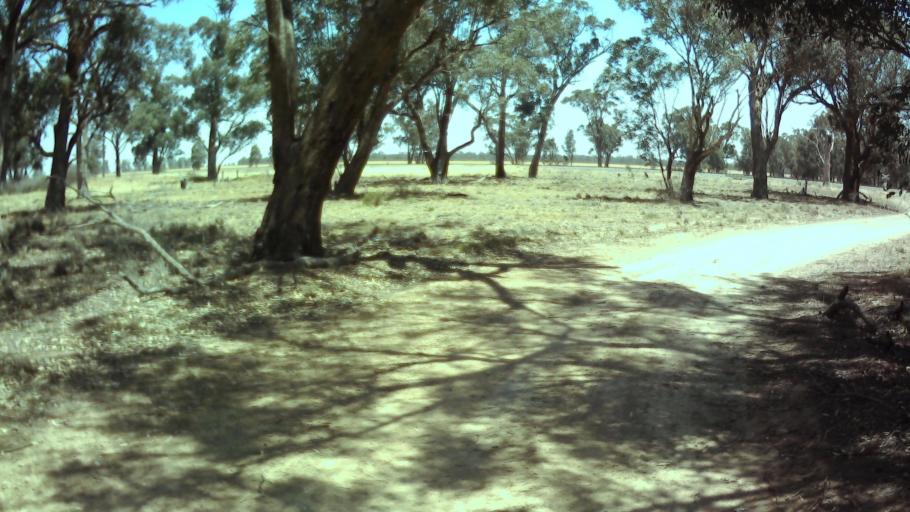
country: AU
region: New South Wales
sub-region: Weddin
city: Grenfell
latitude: -34.0530
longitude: 147.8259
